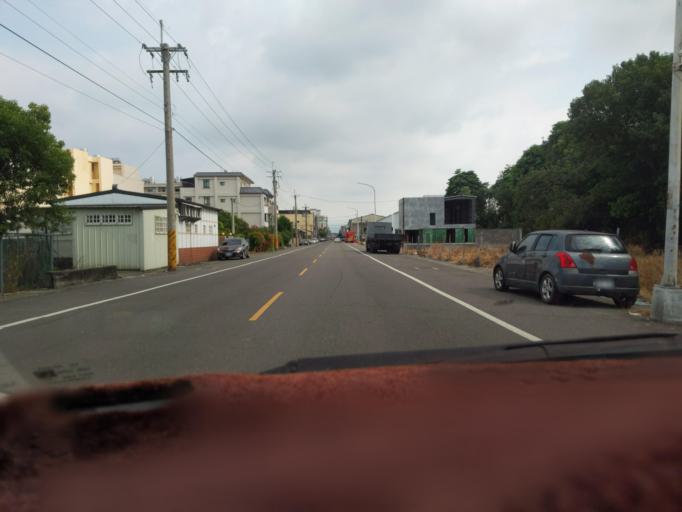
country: TW
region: Taiwan
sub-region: Yunlin
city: Douliu
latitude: 23.8049
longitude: 120.4546
